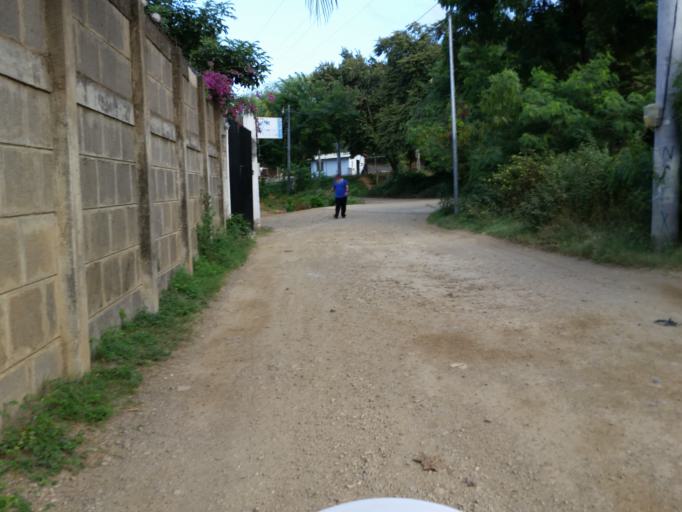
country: NI
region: Rivas
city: San Juan del Sur
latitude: 11.2602
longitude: -85.8742
